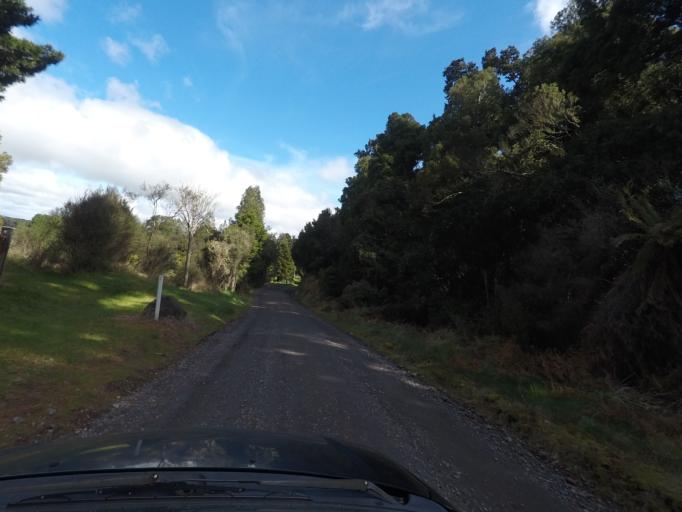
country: NZ
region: Manawatu-Wanganui
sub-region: Ruapehu District
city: Waiouru
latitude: -39.3951
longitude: 175.3972
